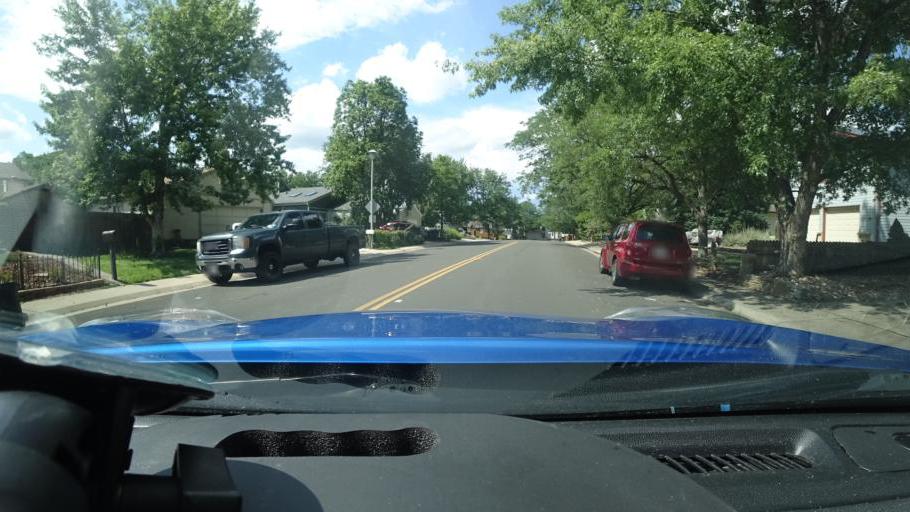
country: US
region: Colorado
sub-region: Adams County
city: Aurora
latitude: 39.6758
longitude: -104.8514
